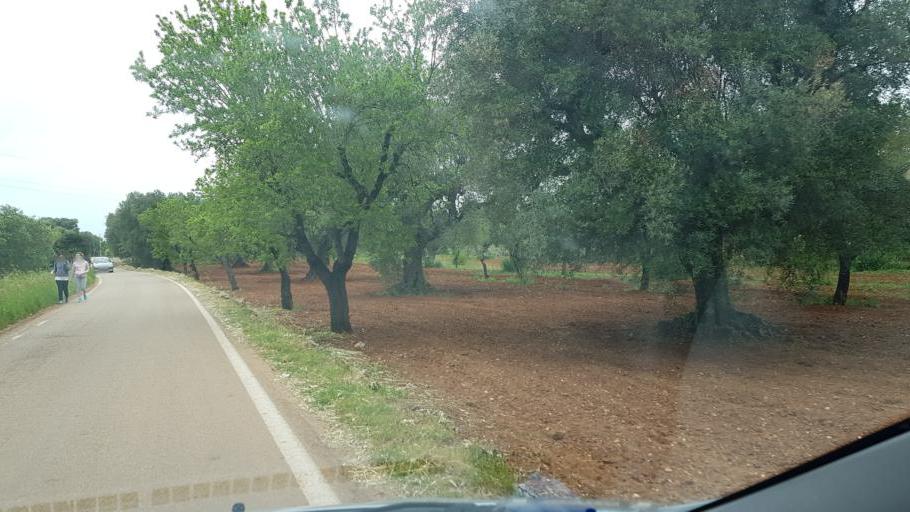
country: IT
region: Apulia
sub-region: Provincia di Brindisi
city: San Vito dei Normanni
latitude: 40.6661
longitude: 17.7467
